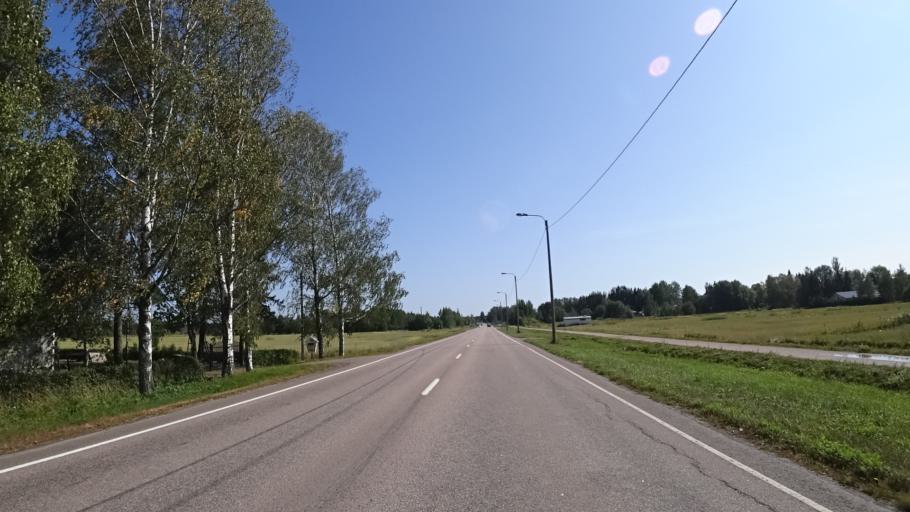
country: FI
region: Kymenlaakso
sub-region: Kotka-Hamina
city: Karhula
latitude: 60.5299
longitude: 26.9396
